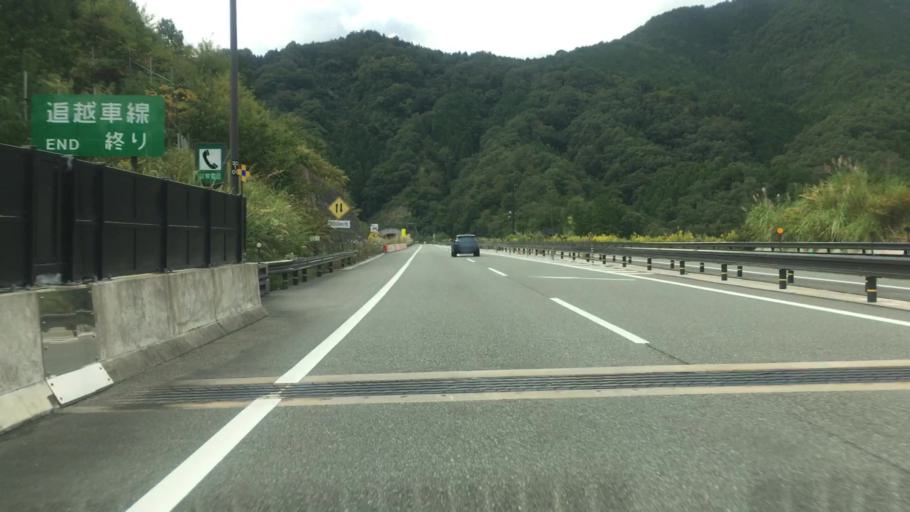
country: JP
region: Hyogo
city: Toyooka
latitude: 35.3436
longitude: 134.8065
